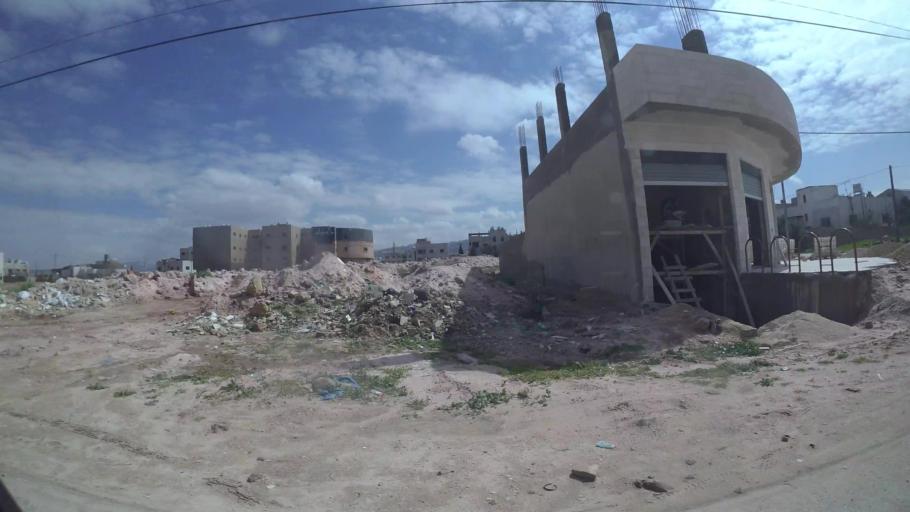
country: JO
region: Amman
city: Al Jubayhah
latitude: 32.0625
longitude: 35.8226
